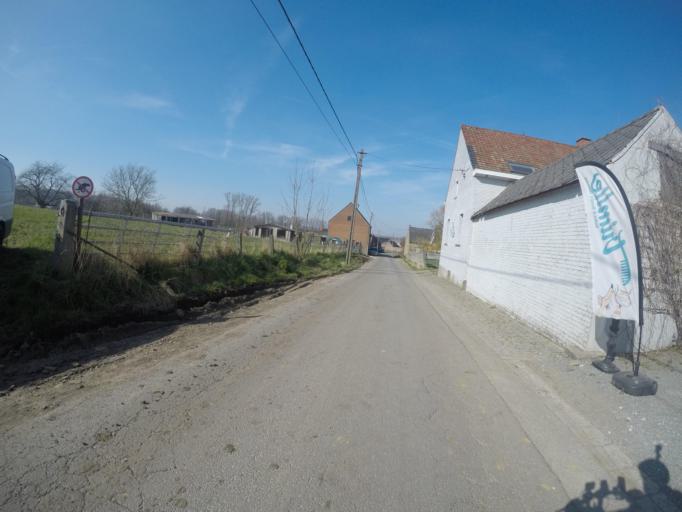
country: BE
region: Flanders
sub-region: Provincie Oost-Vlaanderen
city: Sint-Maria-Lierde
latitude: 50.7814
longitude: 3.8169
